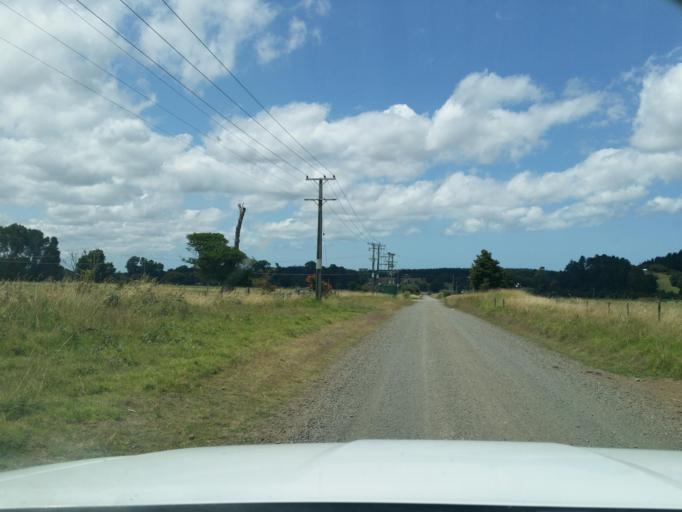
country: NZ
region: Northland
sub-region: Kaipara District
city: Dargaville
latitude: -35.7973
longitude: 173.7317
